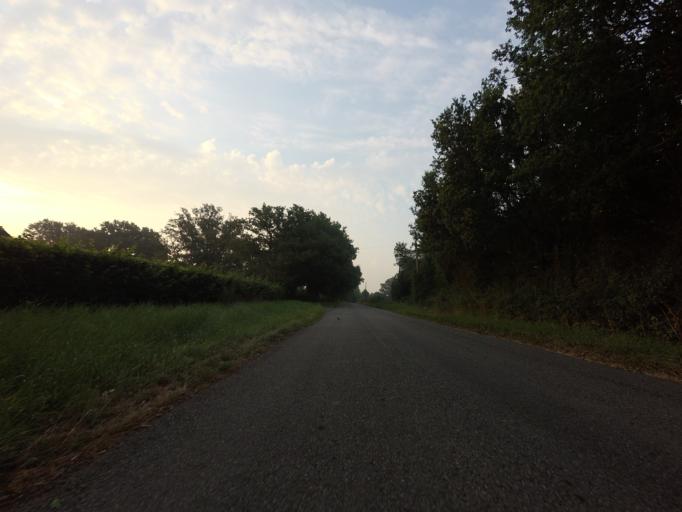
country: GB
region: England
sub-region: Kent
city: Lenham
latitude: 51.1798
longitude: 0.7248
